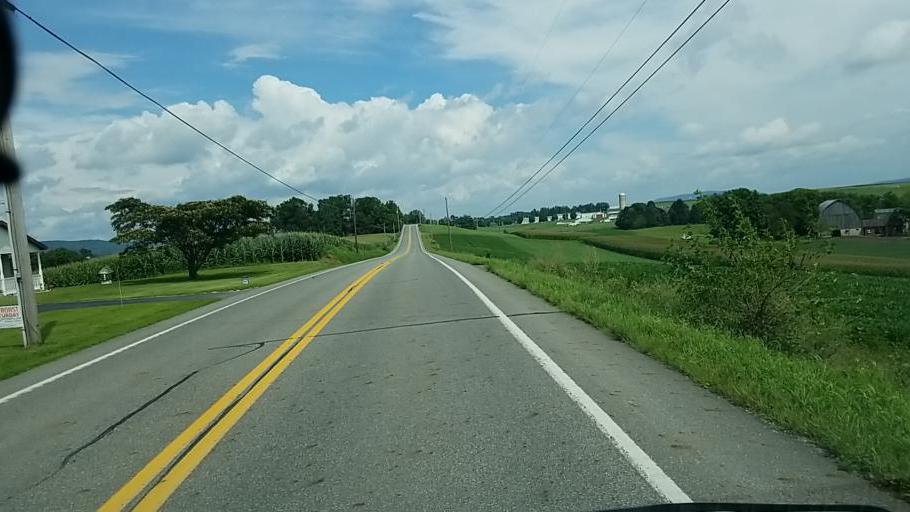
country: US
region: Pennsylvania
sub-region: Dauphin County
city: Elizabethville
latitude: 40.5789
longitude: -76.8834
